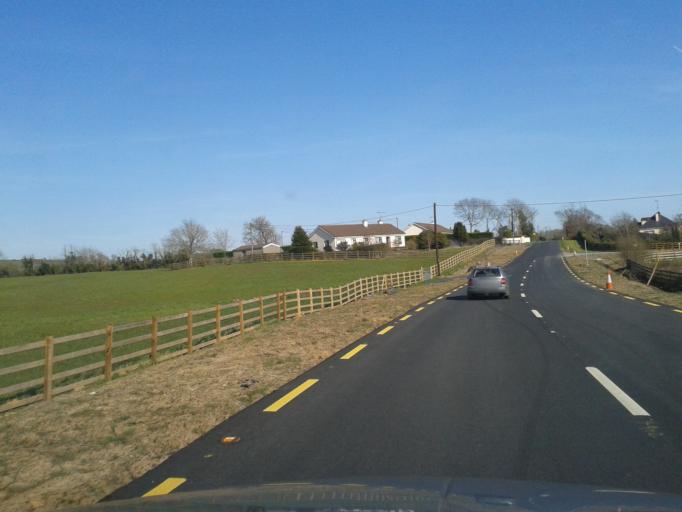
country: IE
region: Leinster
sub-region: Wicklow
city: Arklow
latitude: 52.8828
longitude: -6.0953
